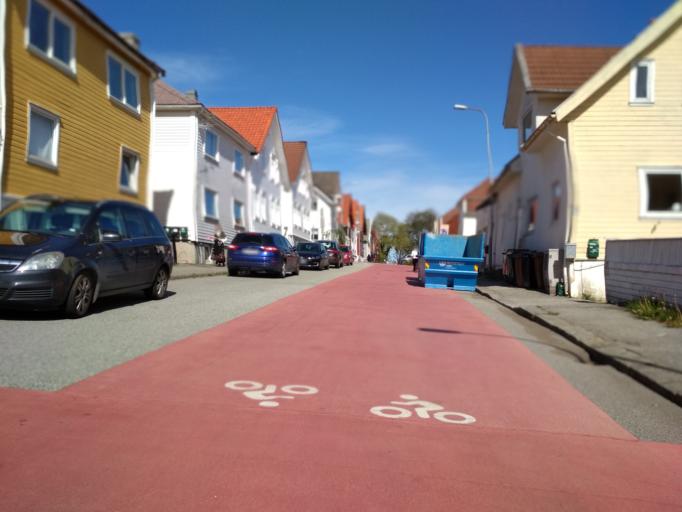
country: NO
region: Rogaland
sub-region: Stavanger
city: Stavanger
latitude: 58.9697
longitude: 5.7238
